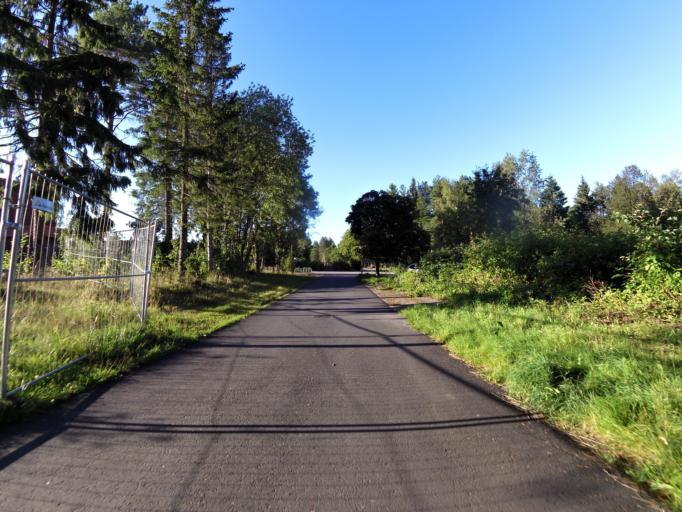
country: SE
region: Gaevleborg
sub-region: Gavle Kommun
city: Gavle
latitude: 60.6507
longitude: 17.1405
